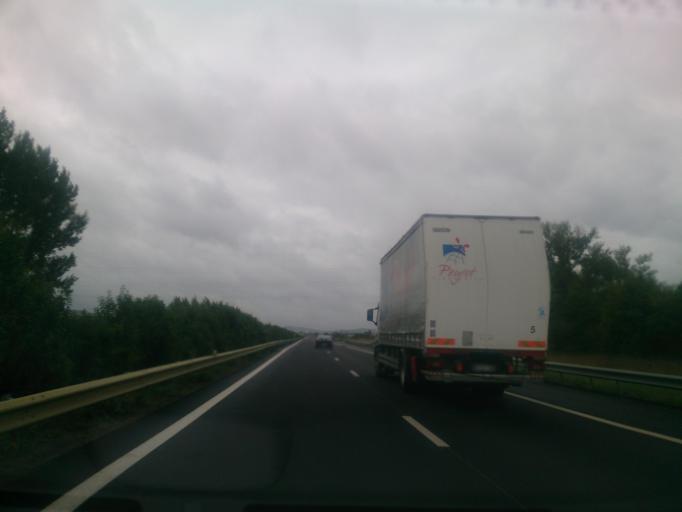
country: FR
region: Midi-Pyrenees
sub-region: Departement de la Haute-Garonne
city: Martres-Tolosane
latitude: 43.2199
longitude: 1.0460
